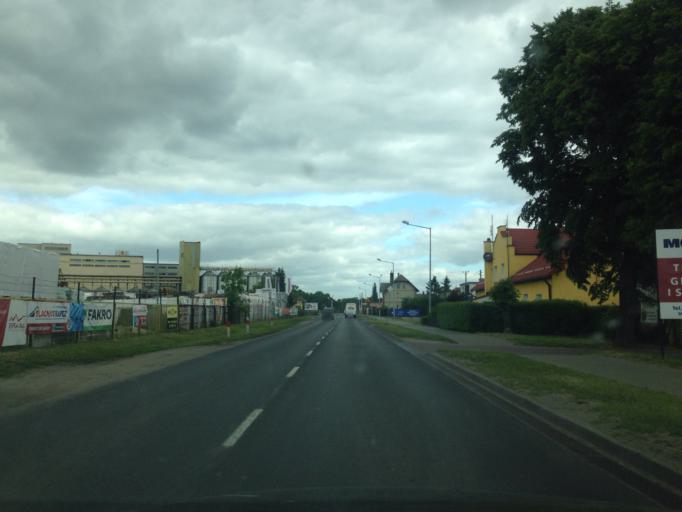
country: PL
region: Kujawsko-Pomorskie
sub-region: Powiat swiecki
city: Swiecie
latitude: 53.3968
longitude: 18.4049
